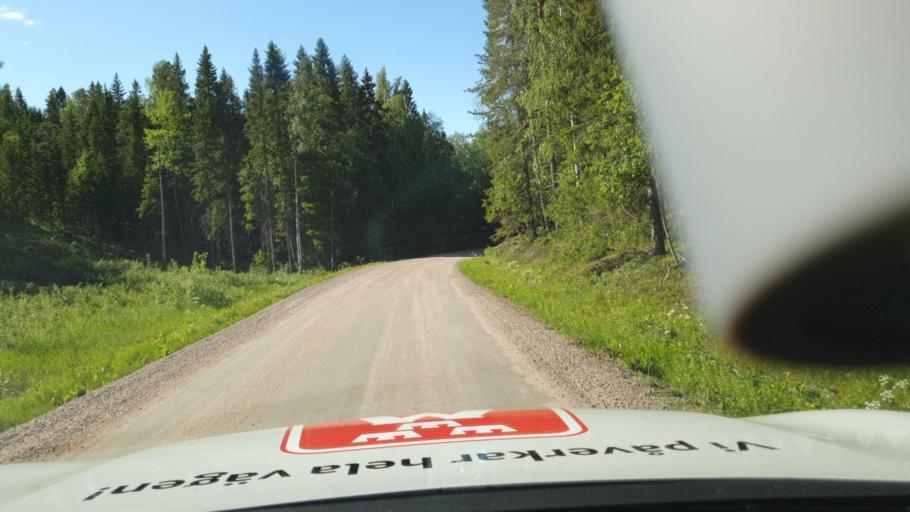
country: SE
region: Vaesterbotten
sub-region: Vannas Kommun
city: Vaennaes
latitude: 63.8445
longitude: 19.6232
